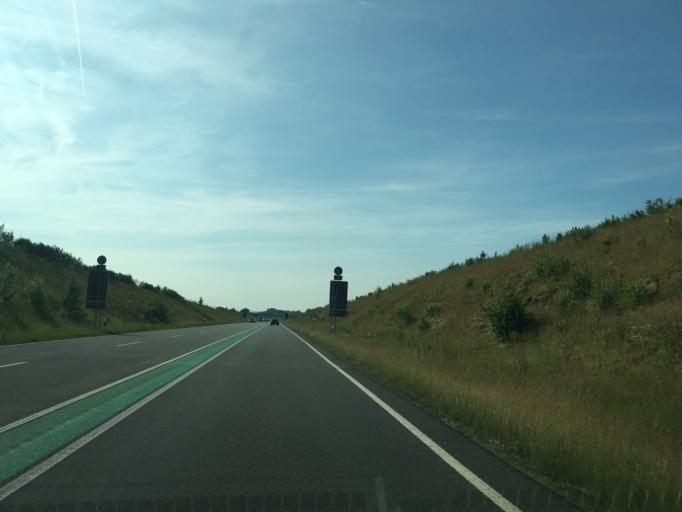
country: DE
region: North Rhine-Westphalia
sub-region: Regierungsbezirk Munster
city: Steinfurt
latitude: 52.1651
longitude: 7.3067
